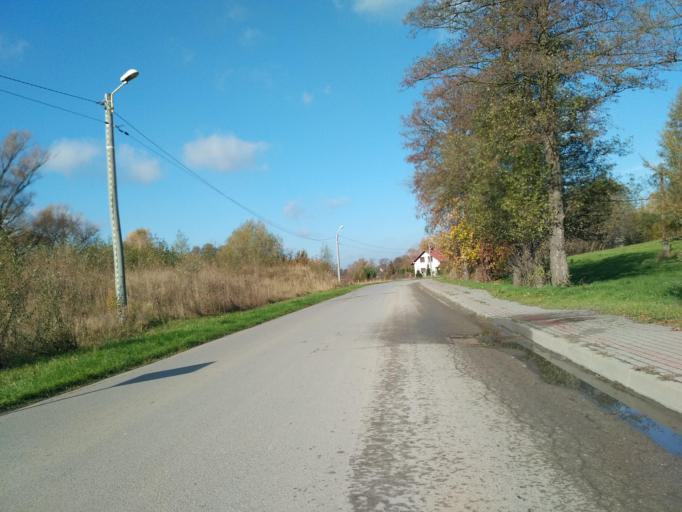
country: PL
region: Subcarpathian Voivodeship
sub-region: Powiat rzeszowski
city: Niechobrz
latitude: 50.0128
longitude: 21.8967
